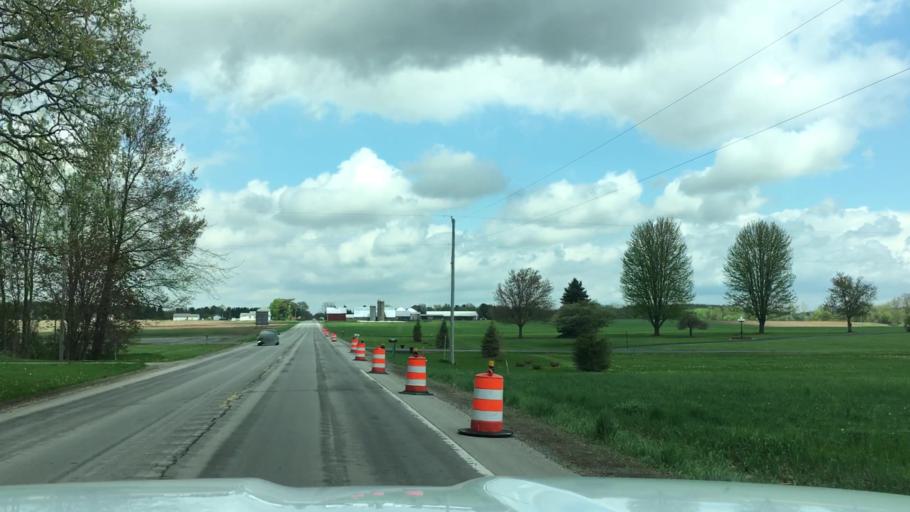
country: US
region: Michigan
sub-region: Ingham County
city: Stockbridge
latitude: 42.4608
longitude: -84.1901
